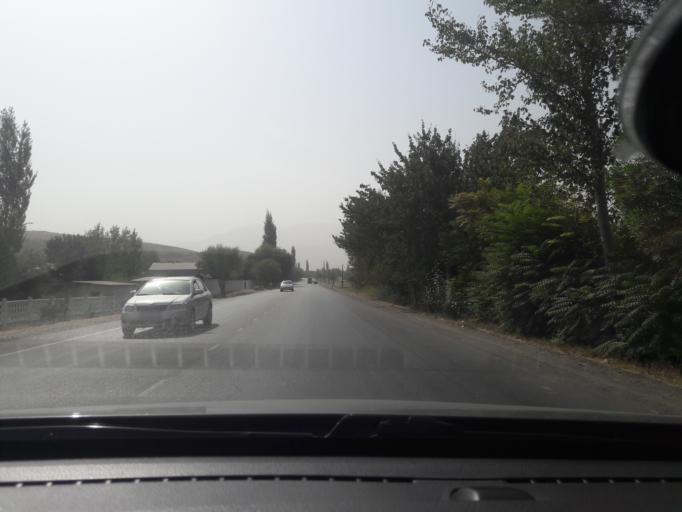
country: TJ
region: Republican Subordination
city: Vahdat
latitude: 38.5251
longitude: 69.0275
